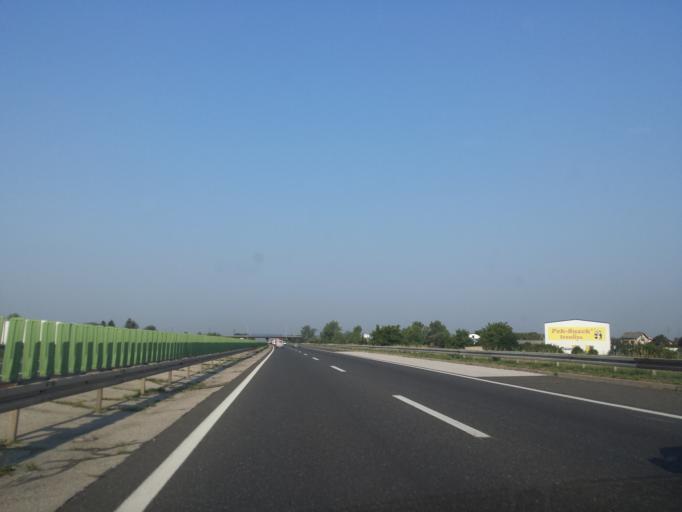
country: HR
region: Grad Zagreb
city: Novi Zagreb
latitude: 45.7530
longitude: 15.9711
